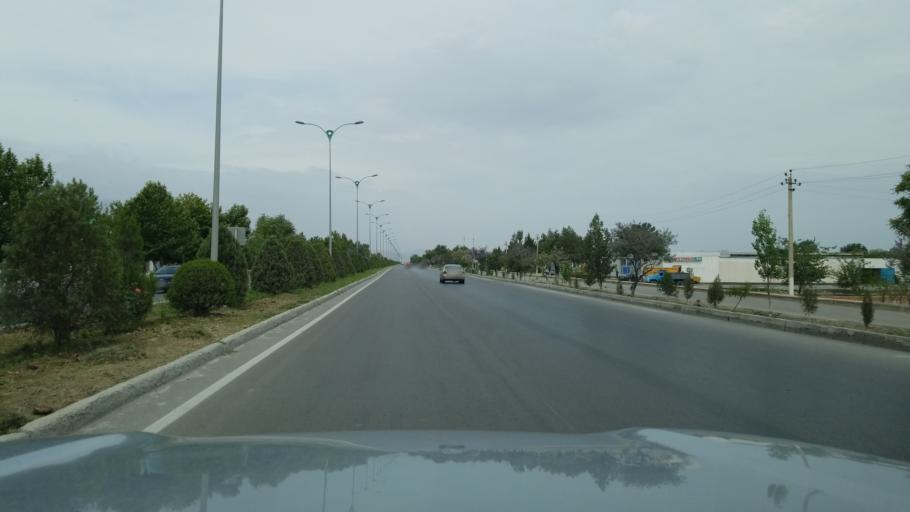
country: TM
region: Ahal
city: Abadan
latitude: 38.1627
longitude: 57.9472
